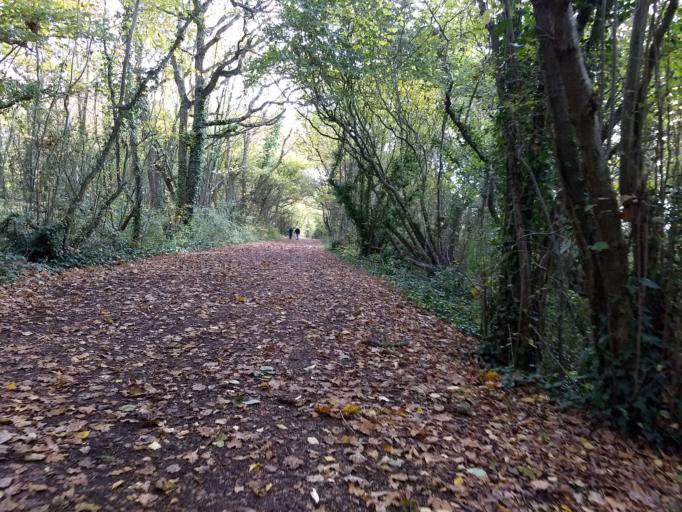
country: GB
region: England
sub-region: Isle of Wight
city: Freshwater
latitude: 50.6889
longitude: -1.5021
